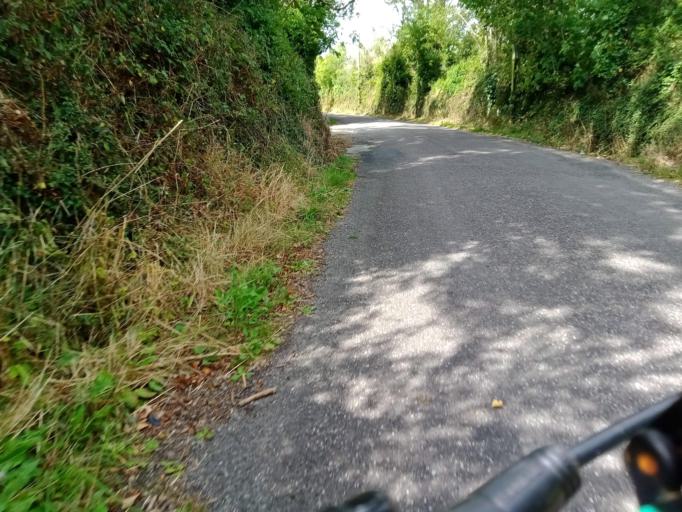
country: IE
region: Munster
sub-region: Waterford
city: Dungarvan
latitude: 52.1392
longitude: -7.4858
